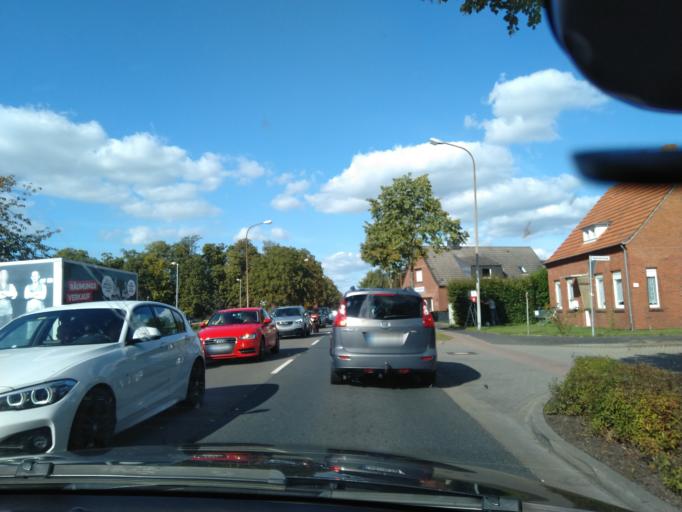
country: DE
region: Lower Saxony
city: Leer
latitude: 53.2450
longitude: 7.4574
